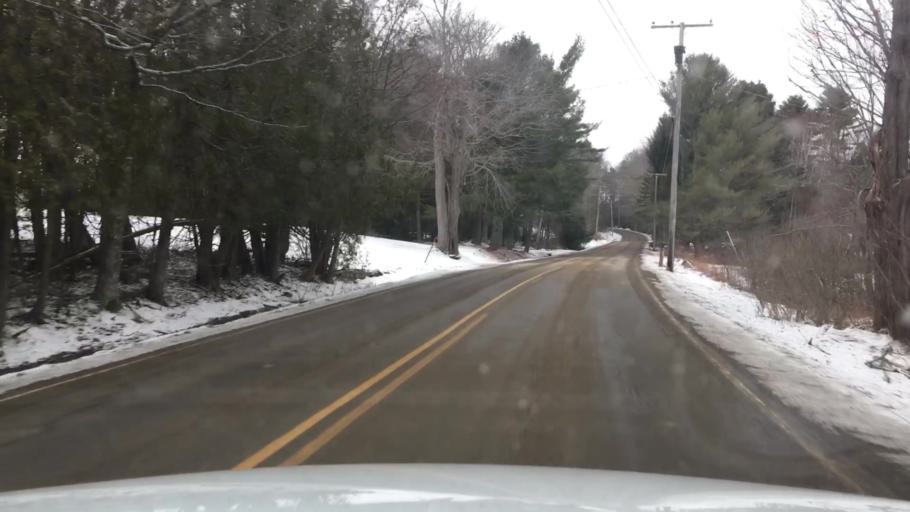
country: US
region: Maine
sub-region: Waldo County
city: Lincolnville
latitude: 44.2843
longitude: -69.0149
